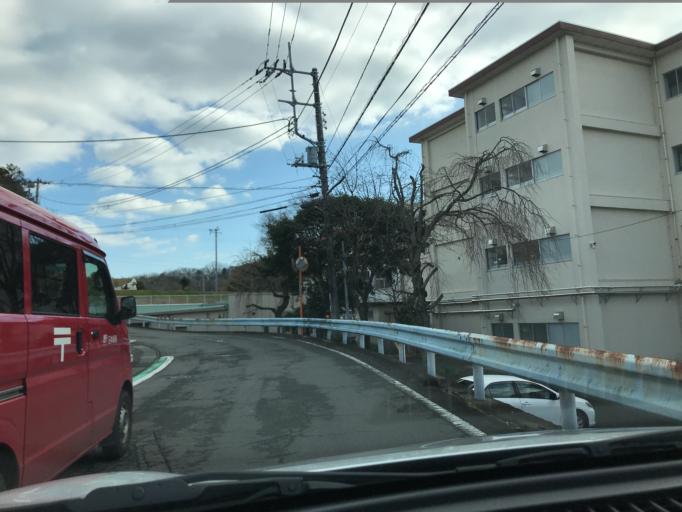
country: JP
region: Shizuoka
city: Mishima
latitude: 35.1049
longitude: 138.9383
